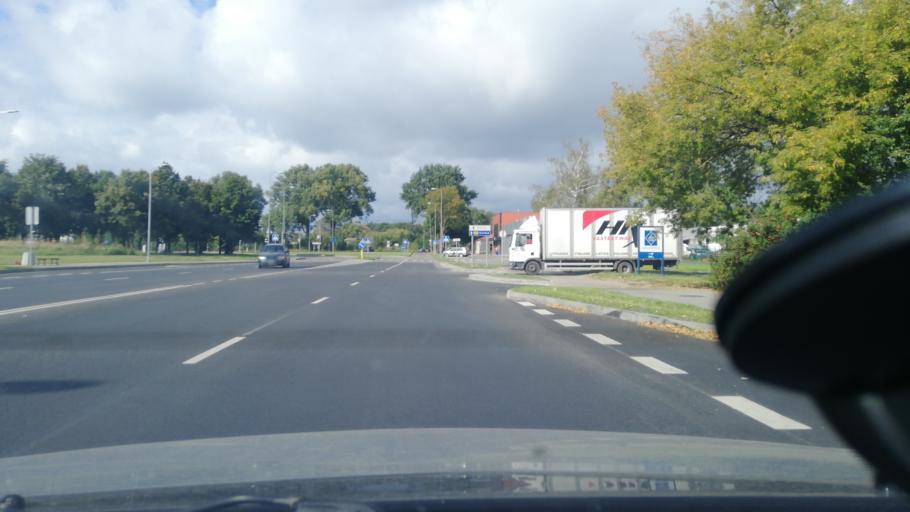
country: LT
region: Klaipedos apskritis
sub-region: Klaipeda
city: Klaipeda
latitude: 55.6659
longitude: 21.1646
